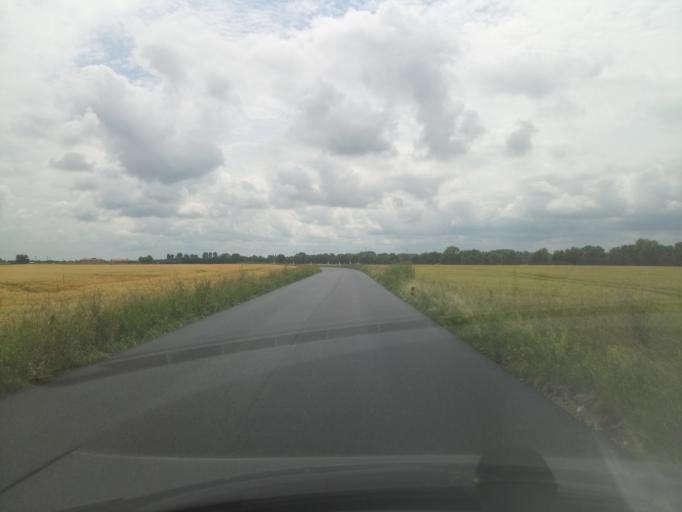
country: FR
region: Poitou-Charentes
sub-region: Departement de la Charente-Maritime
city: Saint-Jean-de-Liversay
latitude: 46.2734
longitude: -0.9032
